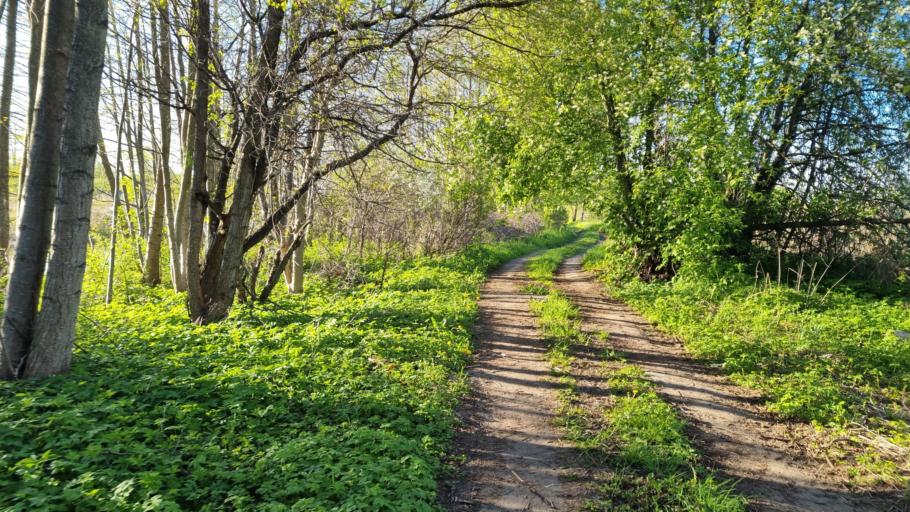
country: LV
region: Riga
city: Bolderaja
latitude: 56.9867
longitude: 24.0587
